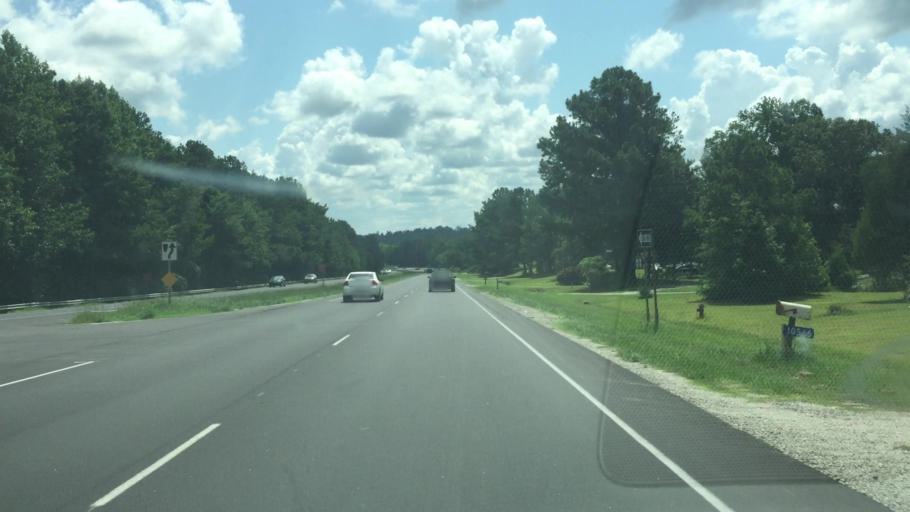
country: US
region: North Carolina
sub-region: Richmond County
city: Cordova
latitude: 34.9460
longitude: -79.8945
